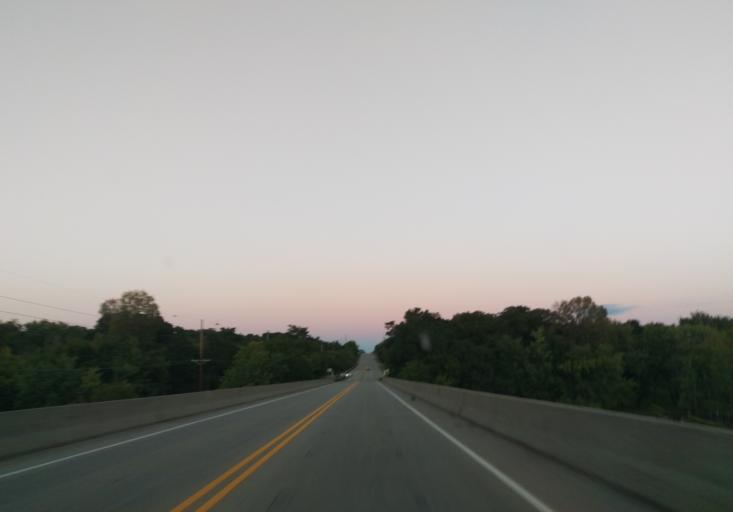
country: US
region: Wisconsin
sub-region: Rock County
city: Janesville
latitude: 42.7301
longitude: -89.0597
